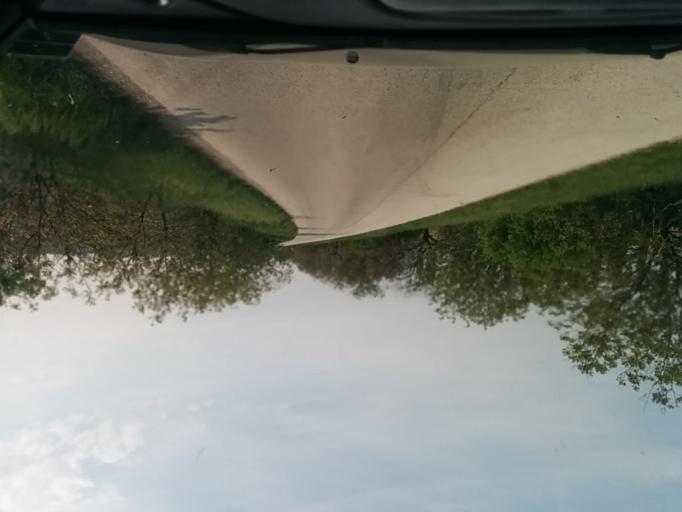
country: SK
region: Trnavsky
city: Sladkovicovo
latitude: 48.2140
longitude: 17.6535
